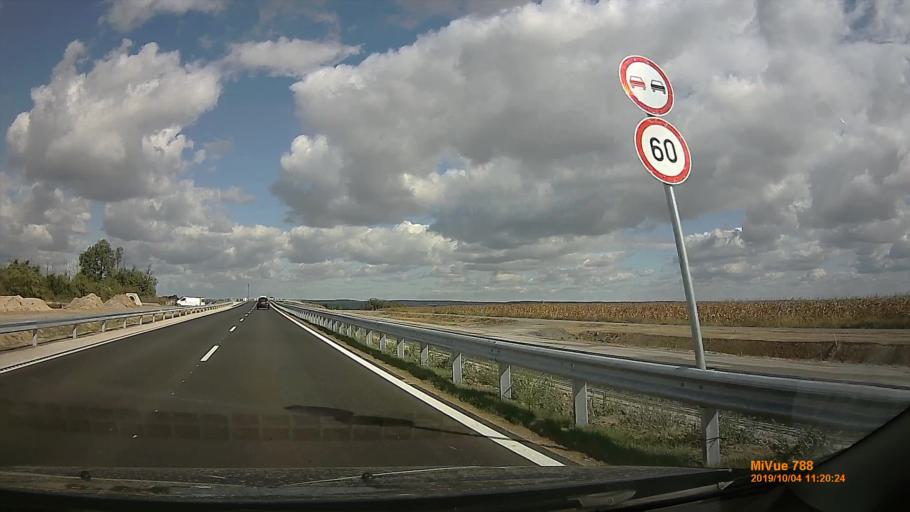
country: HU
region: Somogy
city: Kaposvar
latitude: 46.4968
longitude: 17.8094
